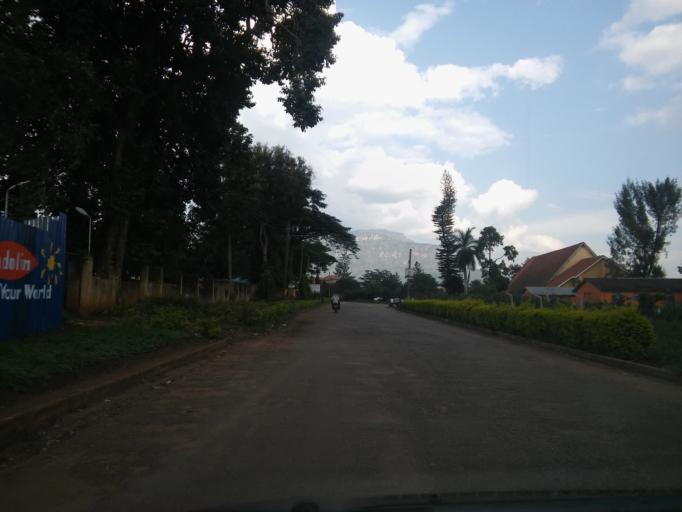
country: UG
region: Eastern Region
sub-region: Mbale District
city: Mbale
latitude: 1.0686
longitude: 34.1826
